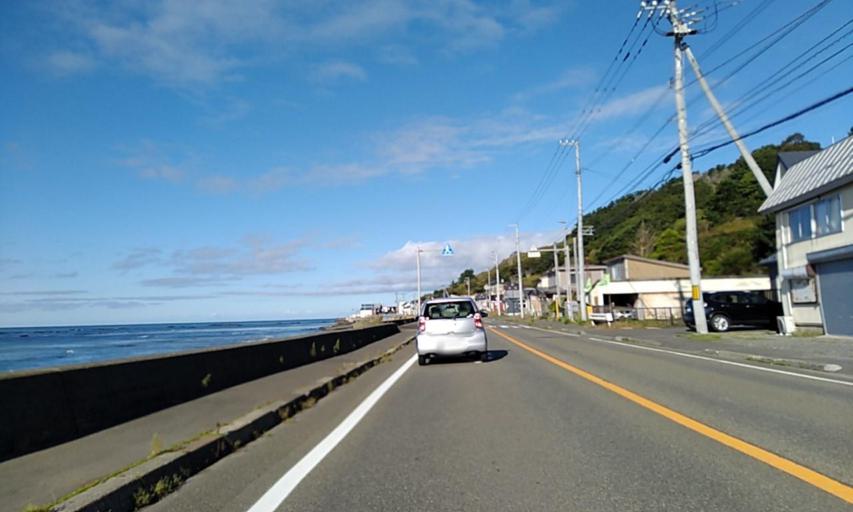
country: JP
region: Hokkaido
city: Shizunai-furukawacho
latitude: 42.1768
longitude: 142.7430
